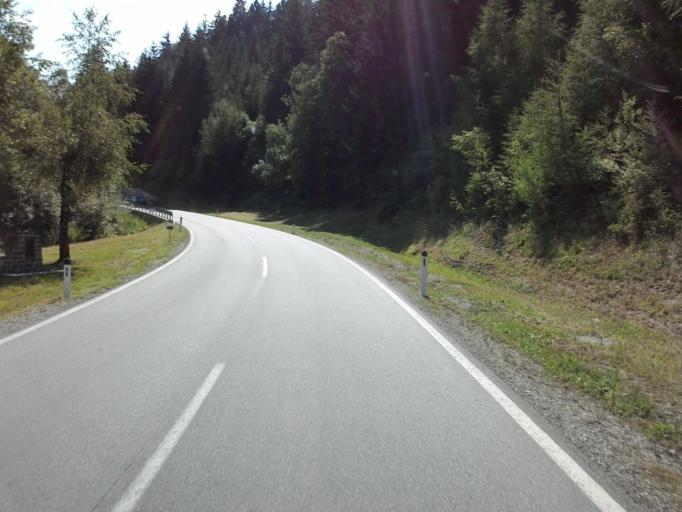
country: AT
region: Tyrol
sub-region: Politischer Bezirk Lienz
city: Strassen
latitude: 46.7430
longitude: 12.4685
